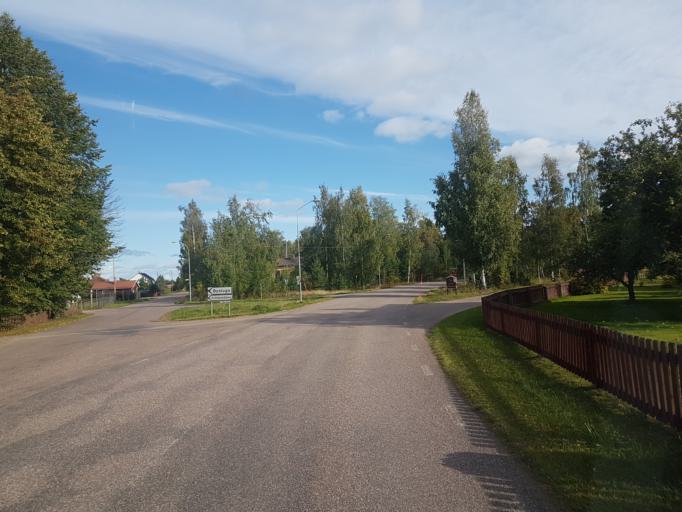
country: SE
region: Dalarna
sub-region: Saters Kommun
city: Saeter
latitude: 60.3910
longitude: 15.6619
